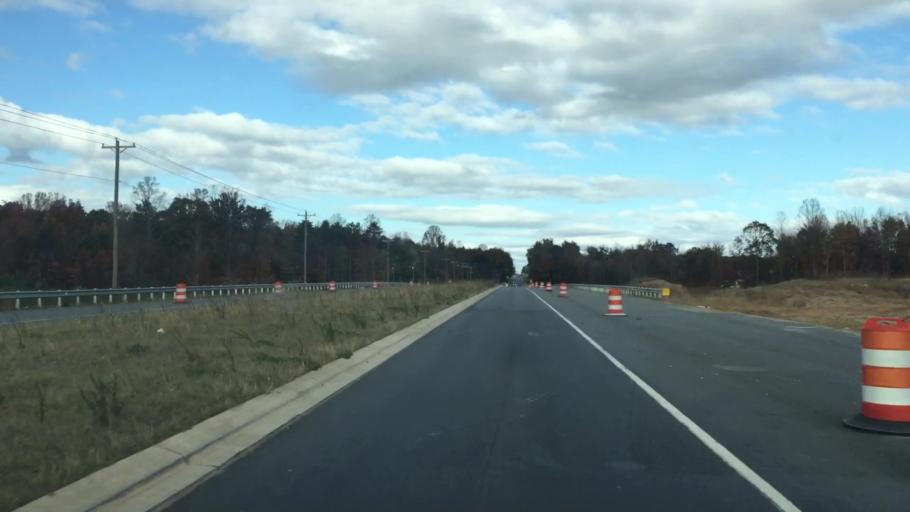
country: US
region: North Carolina
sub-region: Forsyth County
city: Walkertown
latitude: 36.1464
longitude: -80.1560
